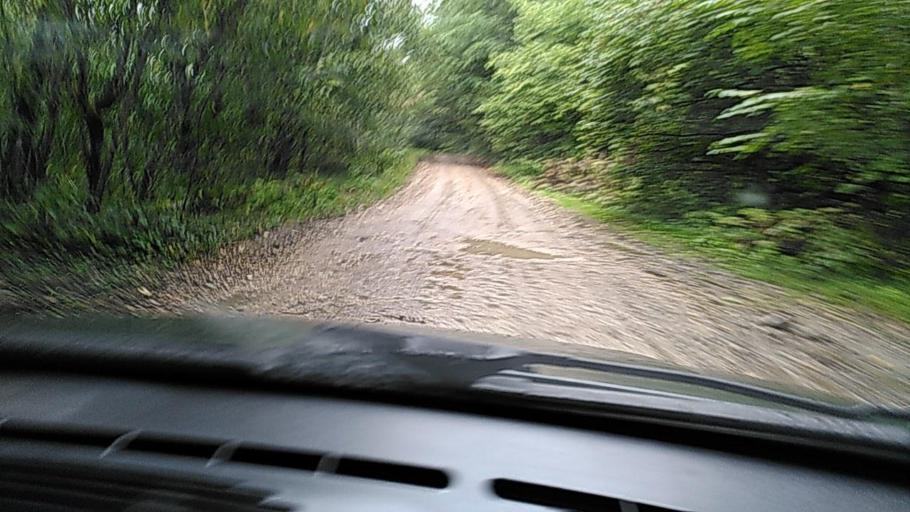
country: RU
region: Kabardino-Balkariya
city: Belaya Rechka
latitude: 43.4001
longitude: 43.4593
